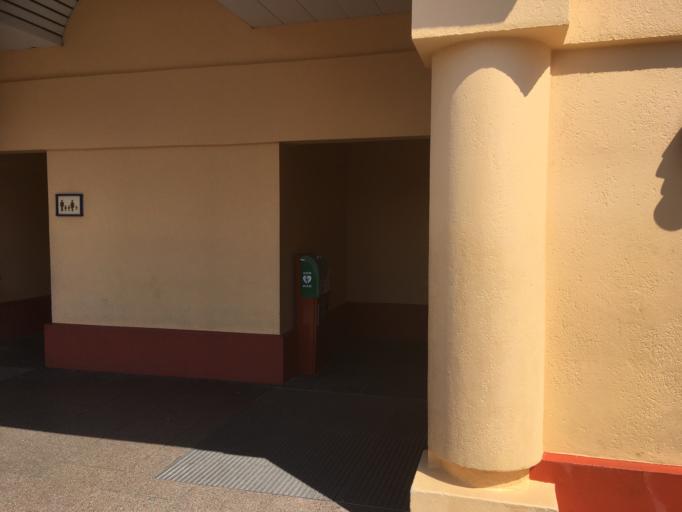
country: FR
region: Ile-de-France
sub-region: Departement de Seine-et-Marne
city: Chalifert
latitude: 48.8727
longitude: 2.7853
